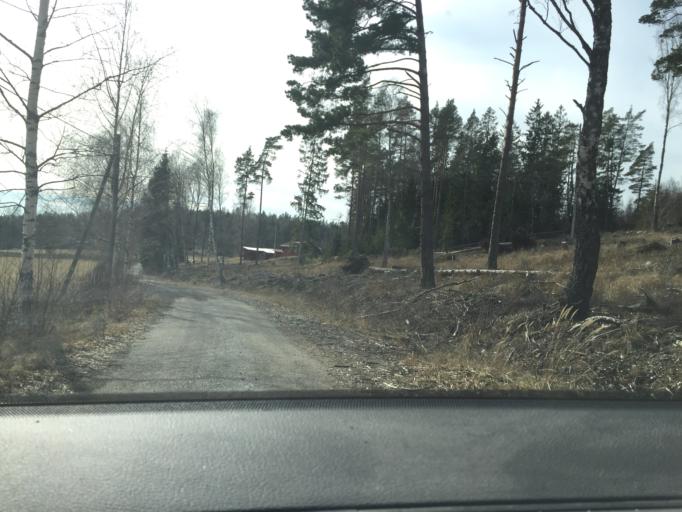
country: SE
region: Stockholm
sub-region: Huddinge Kommun
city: Huddinge
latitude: 59.1330
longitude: 17.9902
